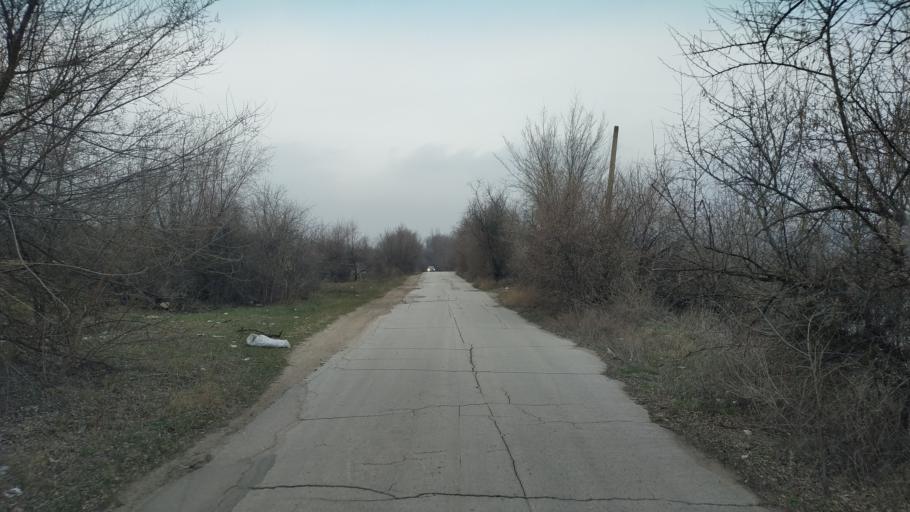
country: MD
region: Chisinau
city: Singera
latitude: 46.9193
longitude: 29.0076
